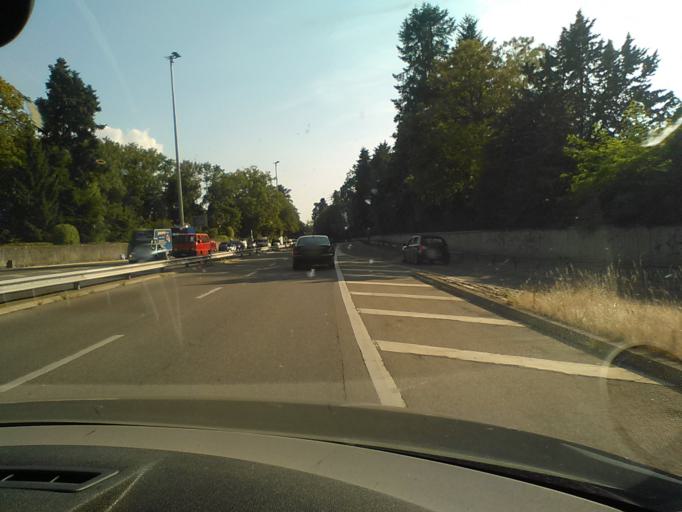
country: CH
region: Geneva
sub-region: Geneva
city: Bellevue
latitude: 46.2419
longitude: 6.1509
